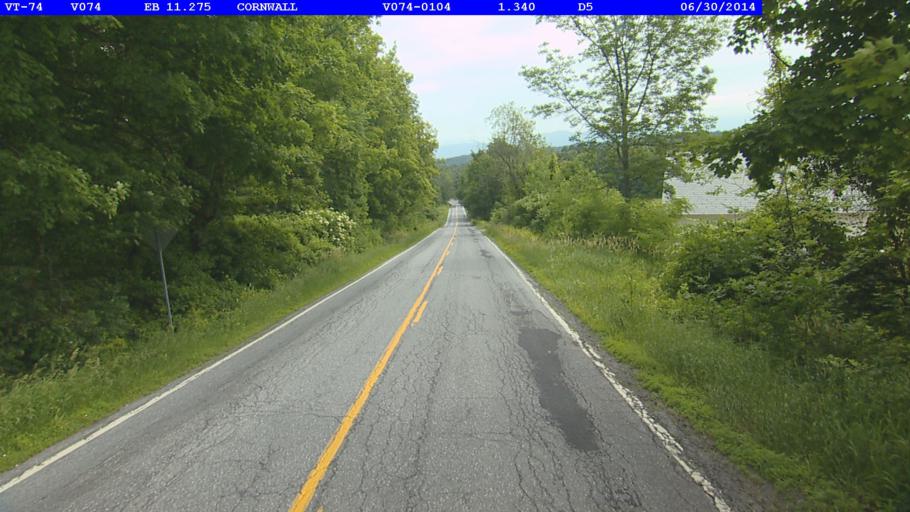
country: US
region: Vermont
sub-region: Addison County
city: Middlebury (village)
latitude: 43.9446
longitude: -73.2314
